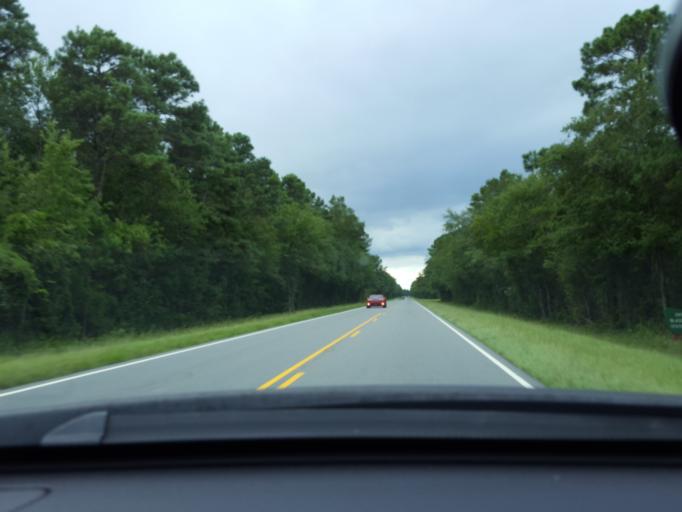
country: US
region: North Carolina
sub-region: Bladen County
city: Elizabethtown
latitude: 34.7316
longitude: -78.4357
